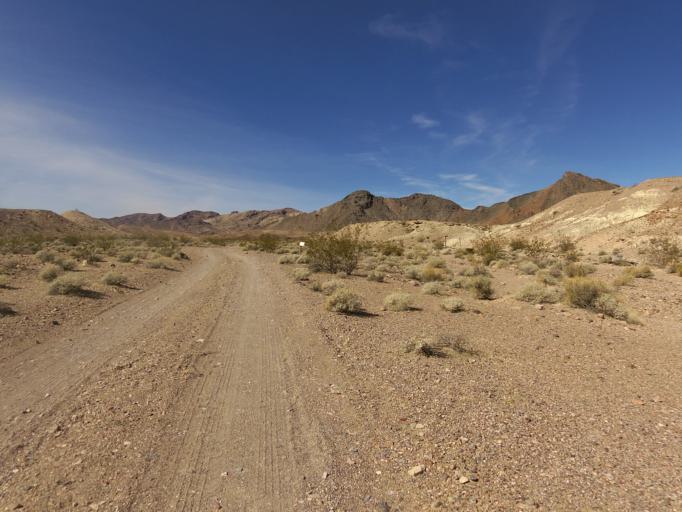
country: US
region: Nevada
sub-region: Nye County
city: Pahrump
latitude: 35.9735
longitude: -116.2770
